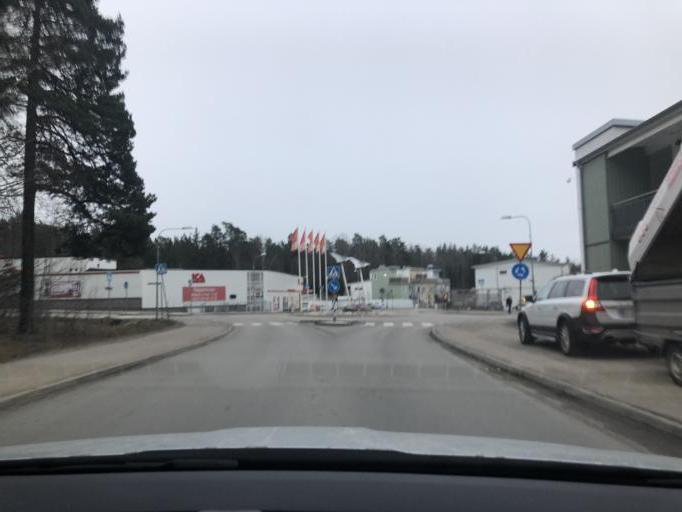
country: SE
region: Stockholm
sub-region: Botkyrka Kommun
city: Tullinge
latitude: 59.1890
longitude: 17.9160
